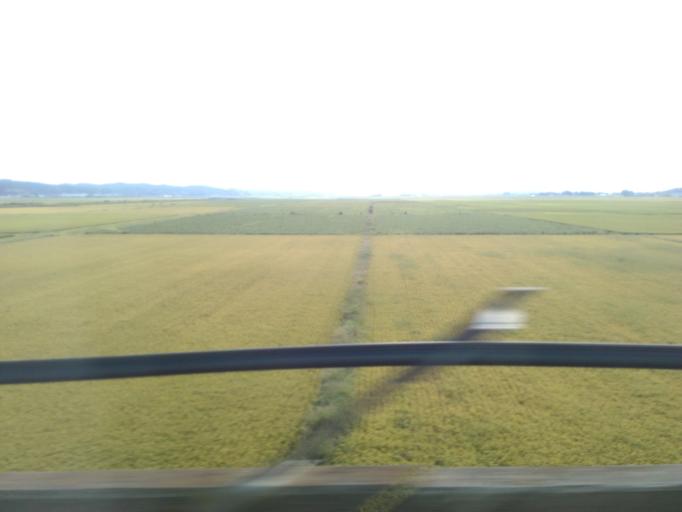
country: JP
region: Iwate
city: Ichinoseki
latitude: 38.7954
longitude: 141.0949
